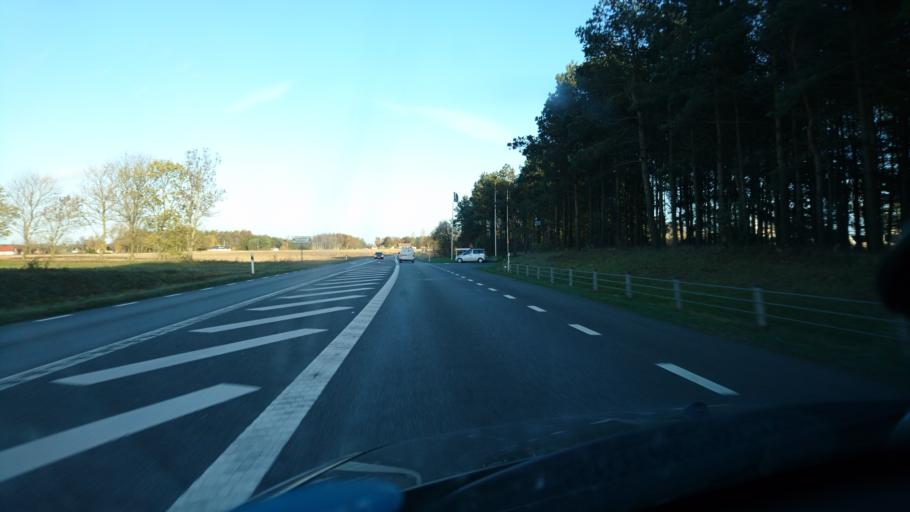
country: SE
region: Skane
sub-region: Tomelilla Kommun
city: Tomelilla
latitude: 55.5528
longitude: 14.0782
